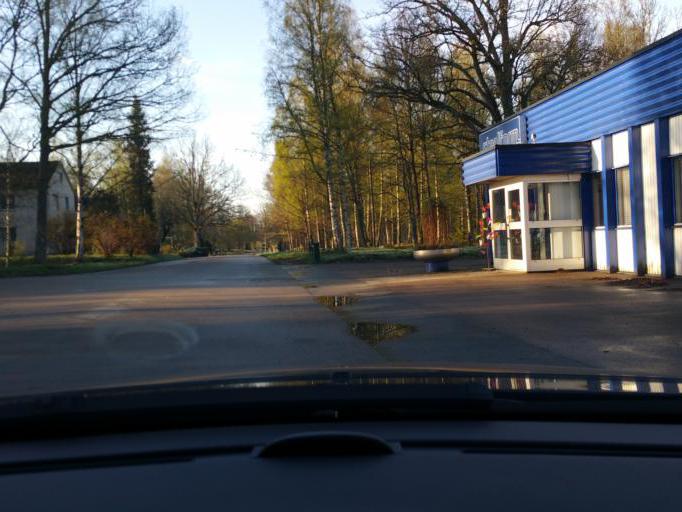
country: SE
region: Kronoberg
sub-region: Vaxjo Kommun
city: Lammhult
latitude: 57.1596
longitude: 14.5871
